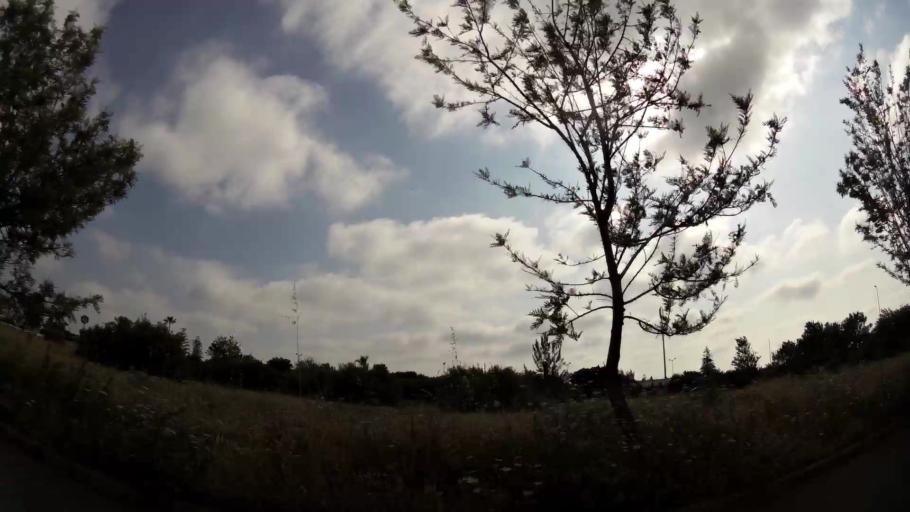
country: MA
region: Rabat-Sale-Zemmour-Zaer
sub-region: Rabat
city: Rabat
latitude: 33.9710
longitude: -6.8500
